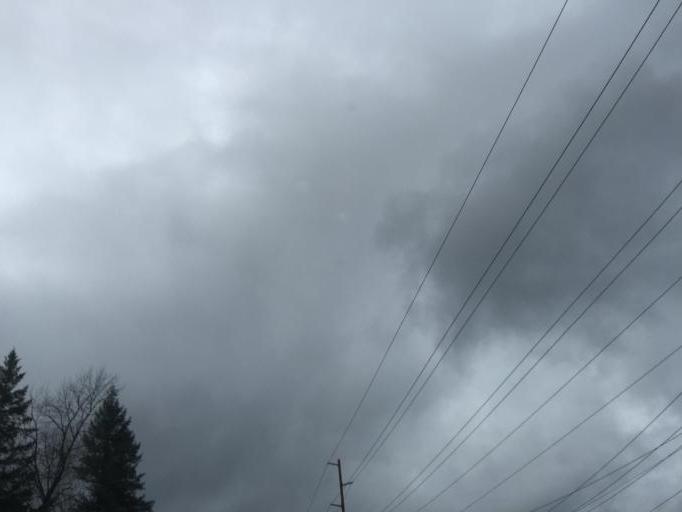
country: US
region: Washington
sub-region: King County
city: Snoqualmie
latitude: 47.5127
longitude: -121.8272
